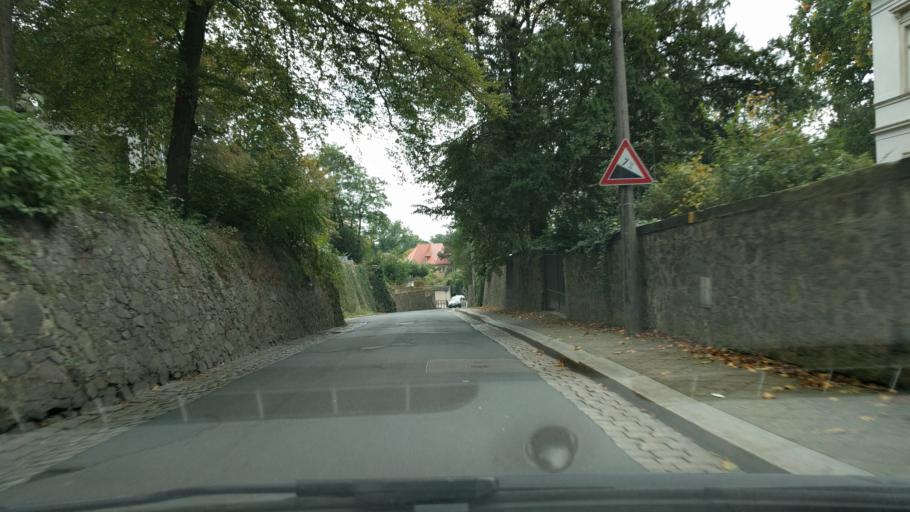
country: DE
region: Saxony
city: Albertstadt
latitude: 51.0607
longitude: 13.8125
